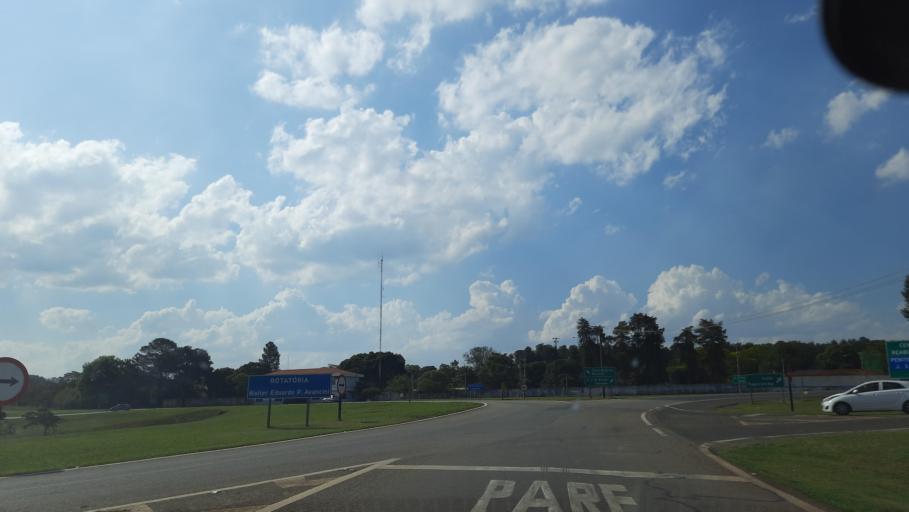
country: BR
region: Sao Paulo
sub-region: Casa Branca
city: Casa Branca
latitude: -21.7743
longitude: -47.0594
